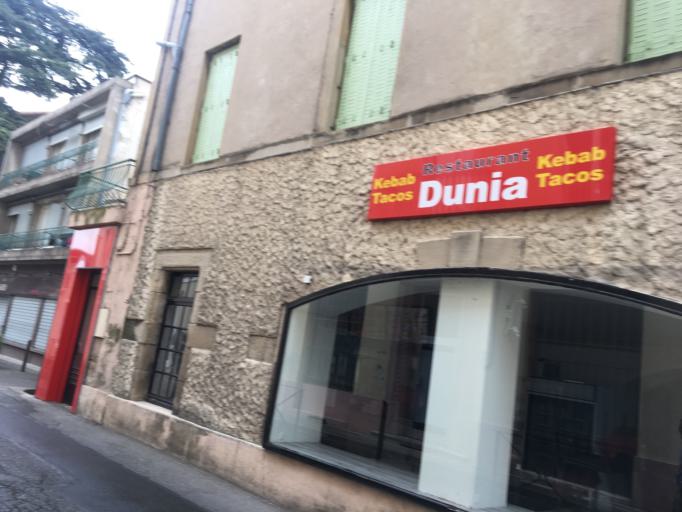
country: FR
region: Rhone-Alpes
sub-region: Departement de l'Ardeche
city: Tournon-sur-Rhone
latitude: 45.0673
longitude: 4.8339
